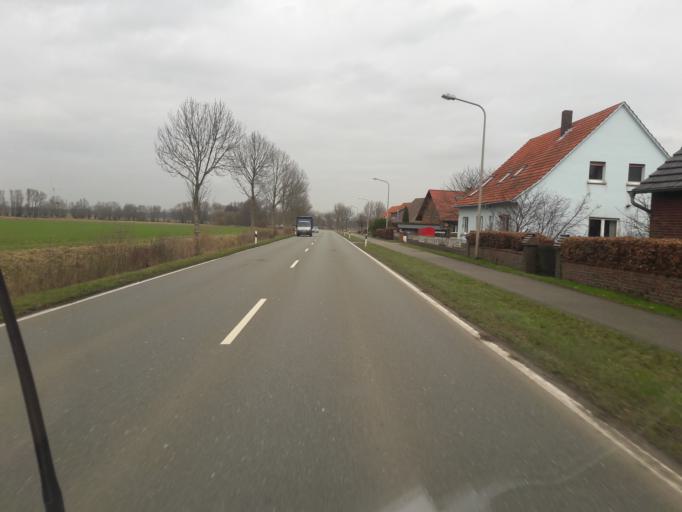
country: DE
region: North Rhine-Westphalia
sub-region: Regierungsbezirk Detmold
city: Hille
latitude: 52.2924
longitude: 8.7994
